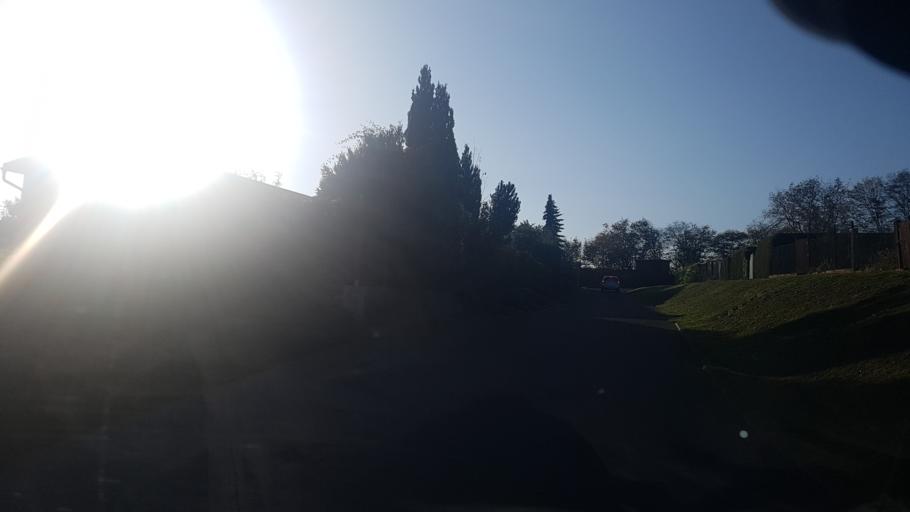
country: DE
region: Saxony
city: Dahlen
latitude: 51.3621
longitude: 12.9983
